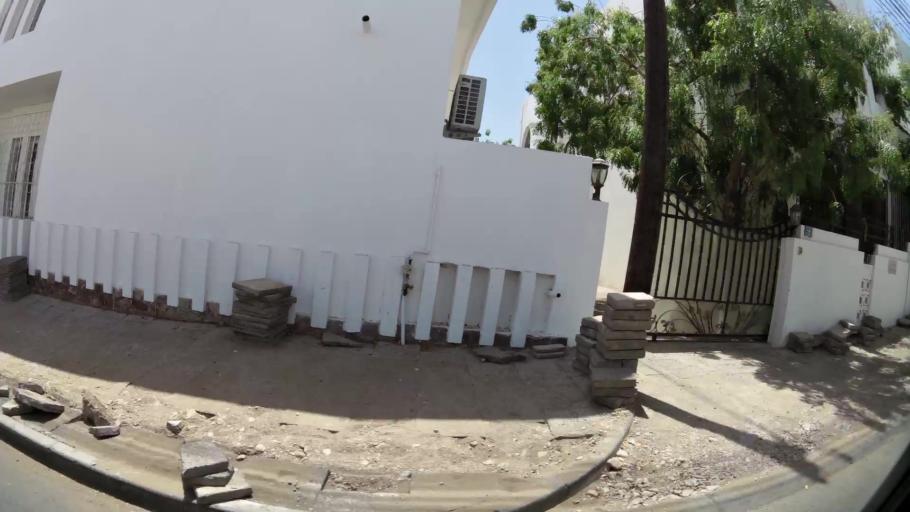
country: OM
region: Muhafazat Masqat
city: Muscat
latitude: 23.6205
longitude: 58.4985
